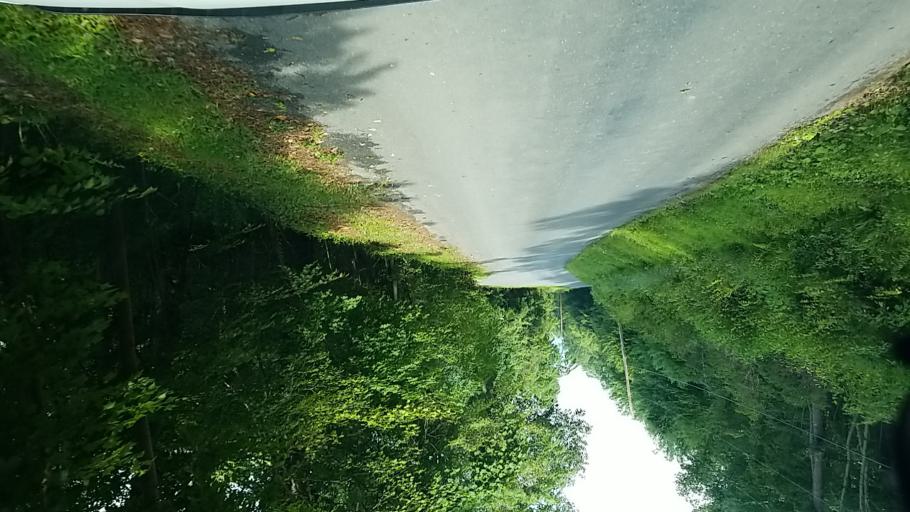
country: US
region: Pennsylvania
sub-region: Dauphin County
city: Millersburg
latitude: 40.5263
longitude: -76.9503
